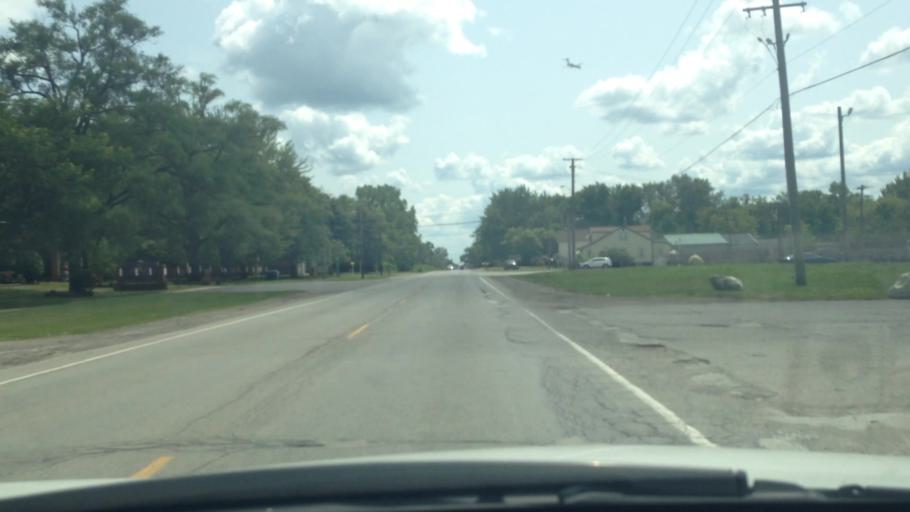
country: US
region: Michigan
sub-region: Wayne County
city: Inkster
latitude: 42.2622
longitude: -83.3088
